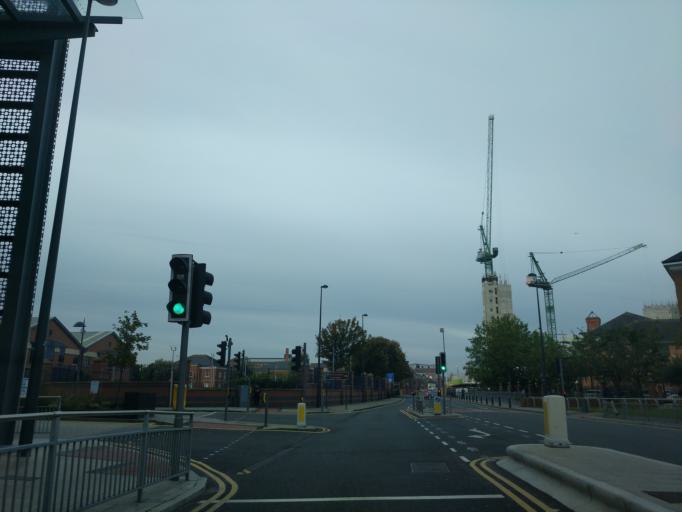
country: GB
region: England
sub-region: City and Borough of Leeds
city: Leeds
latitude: 53.7922
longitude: -1.5482
